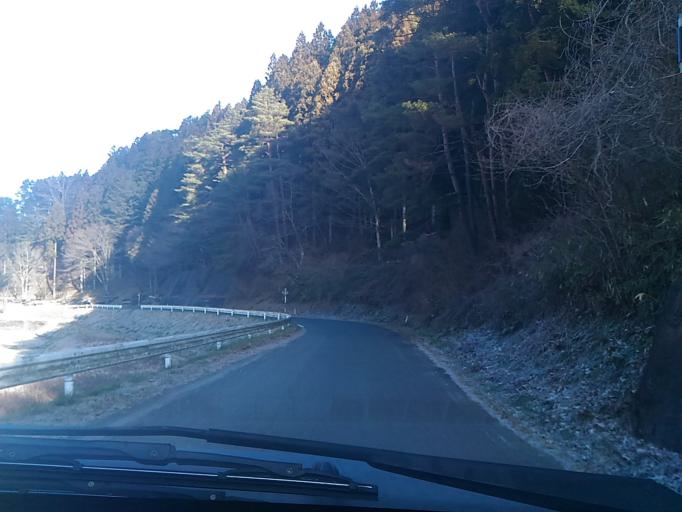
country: JP
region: Fukushima
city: Ishikawa
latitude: 37.0130
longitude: 140.5345
